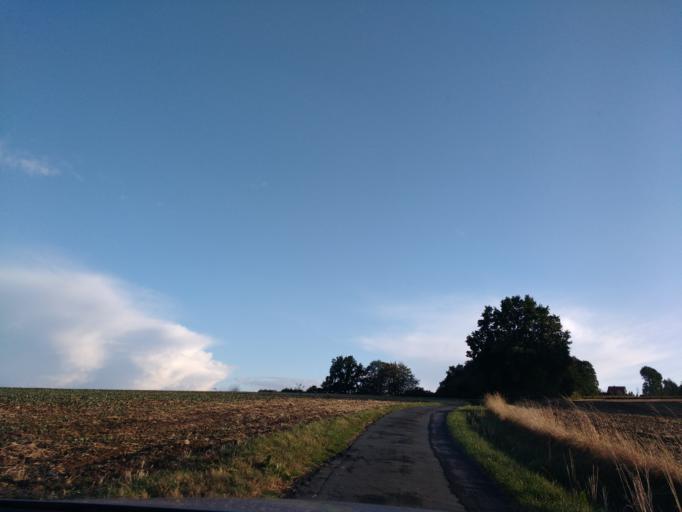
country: DE
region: North Rhine-Westphalia
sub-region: Regierungsbezirk Detmold
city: Detmold
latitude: 51.9648
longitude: 8.9182
